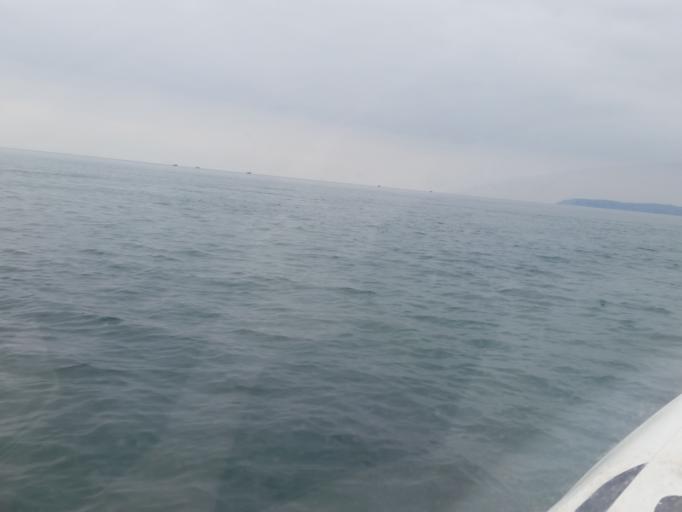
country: IE
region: Leinster
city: Portraine
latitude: 53.4882
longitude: -6.0440
